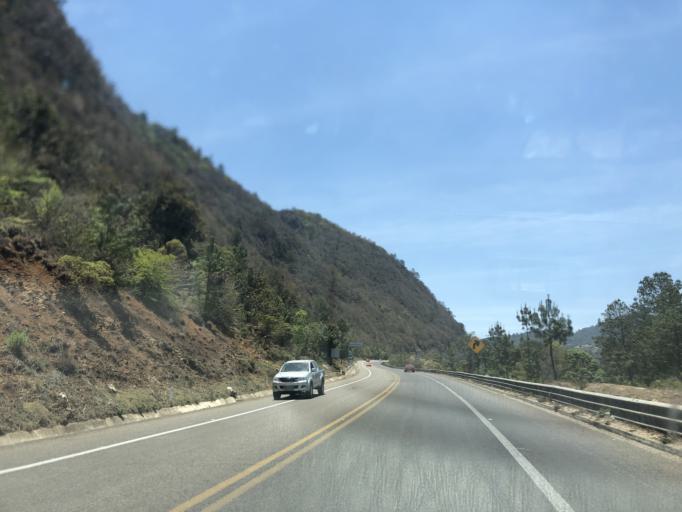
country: MX
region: Chiapas
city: San Cristobal de las Casas
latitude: 16.7194
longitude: -92.6642
